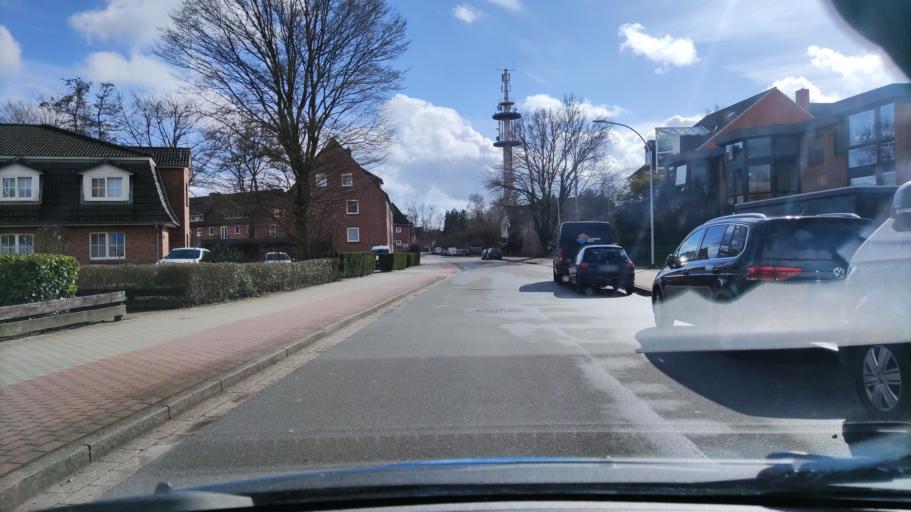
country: DE
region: Lower Saxony
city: Winsen
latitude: 53.3584
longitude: 10.2080
